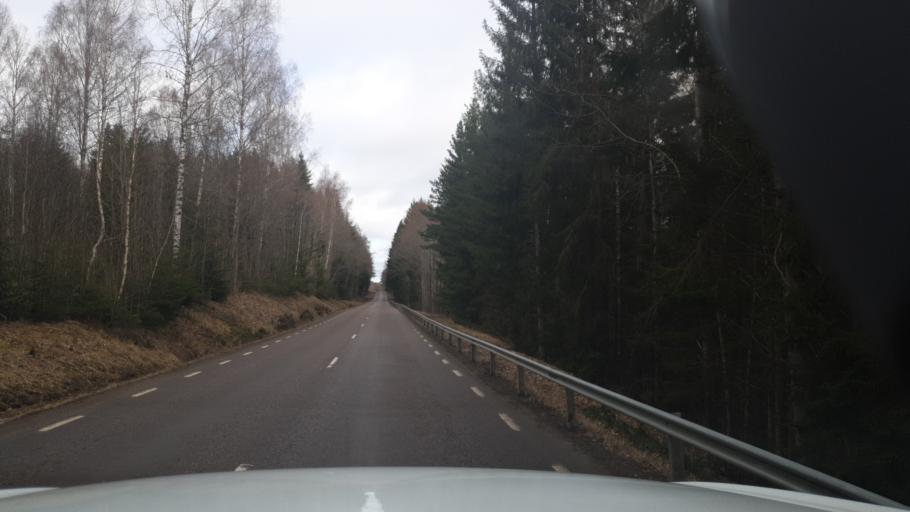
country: SE
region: Vaermland
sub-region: Arvika Kommun
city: Arvika
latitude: 59.6277
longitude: 12.8879
